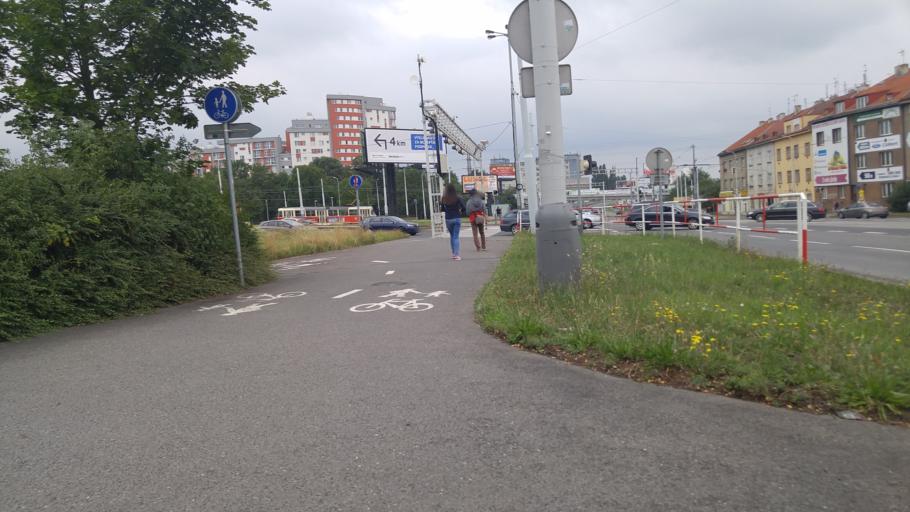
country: CZ
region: Praha
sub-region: Praha 9
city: Vysocany
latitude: 50.1049
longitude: 14.5319
